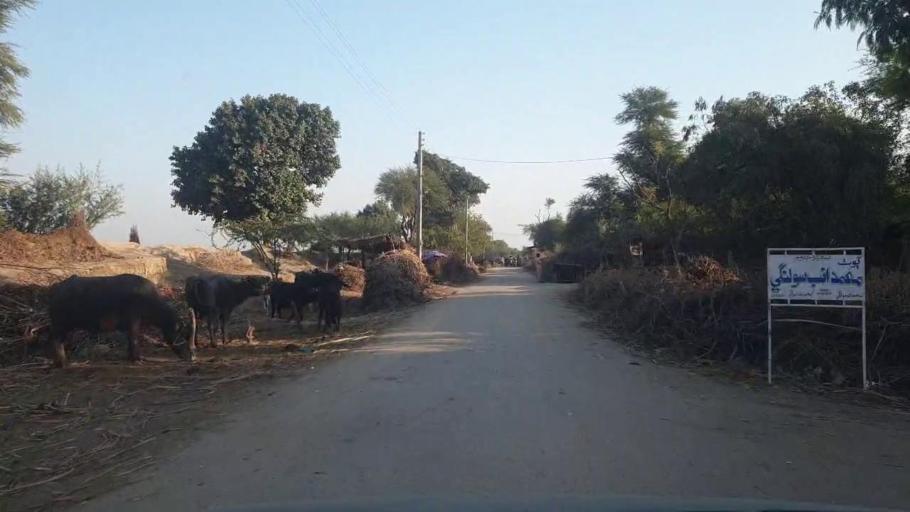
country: PK
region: Sindh
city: Chambar
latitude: 25.2883
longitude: 68.8964
